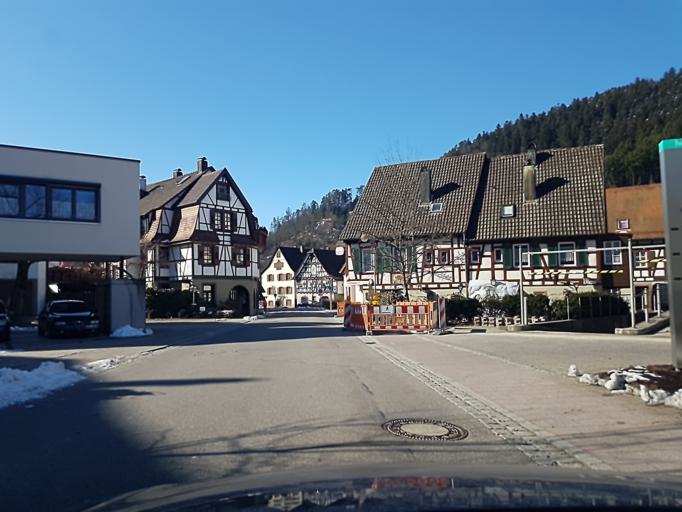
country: DE
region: Baden-Wuerttemberg
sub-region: Freiburg Region
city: Schiltach
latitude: 48.2903
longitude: 8.3460
